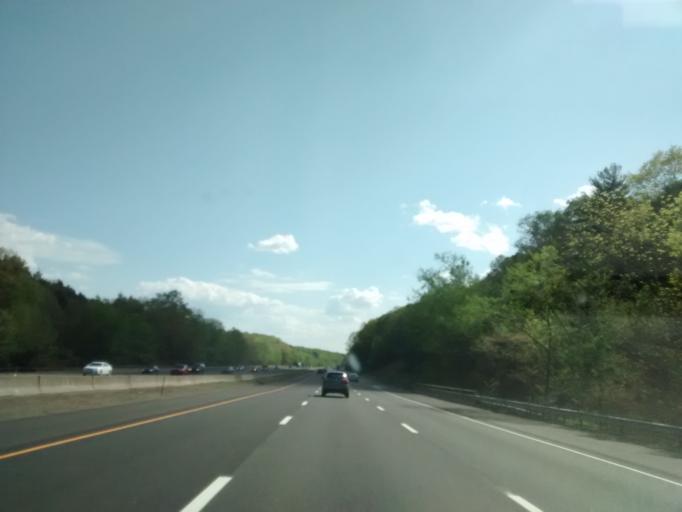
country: US
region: Connecticut
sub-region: Tolland County
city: Stafford Springs
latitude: 41.9173
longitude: -72.2651
